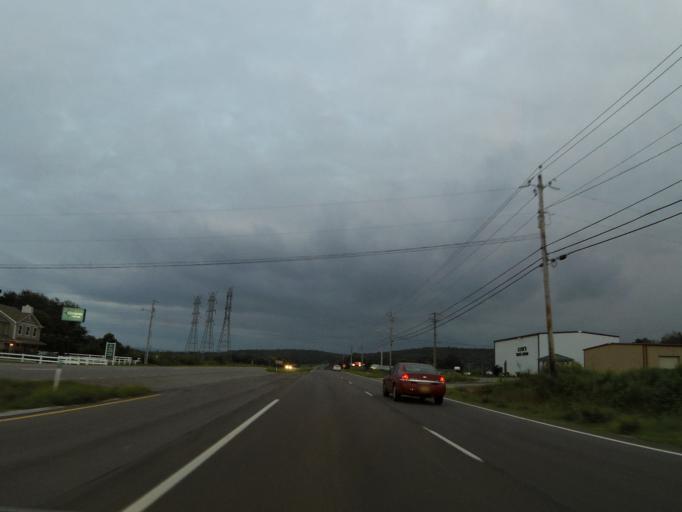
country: US
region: Alabama
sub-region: Madison County
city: Moores Mill
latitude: 34.7717
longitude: -86.5110
